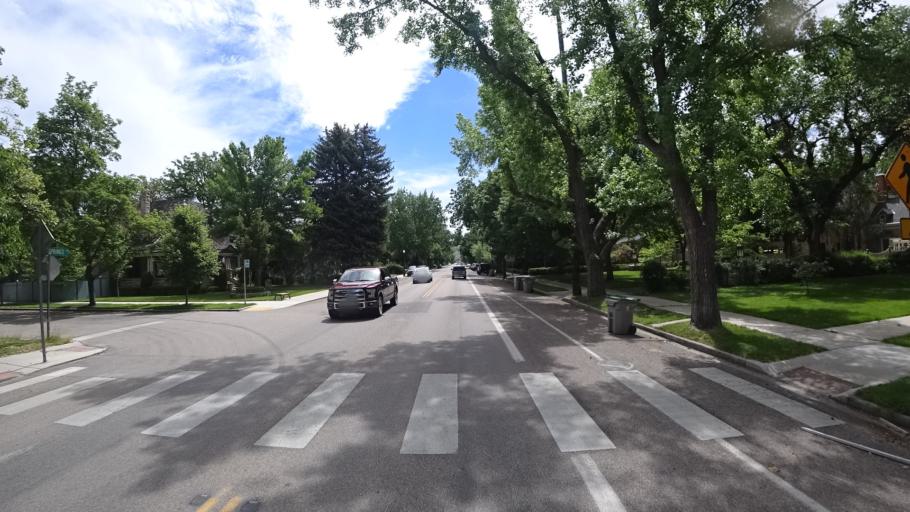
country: US
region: Idaho
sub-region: Ada County
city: Boise
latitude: 43.6083
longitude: -116.1855
